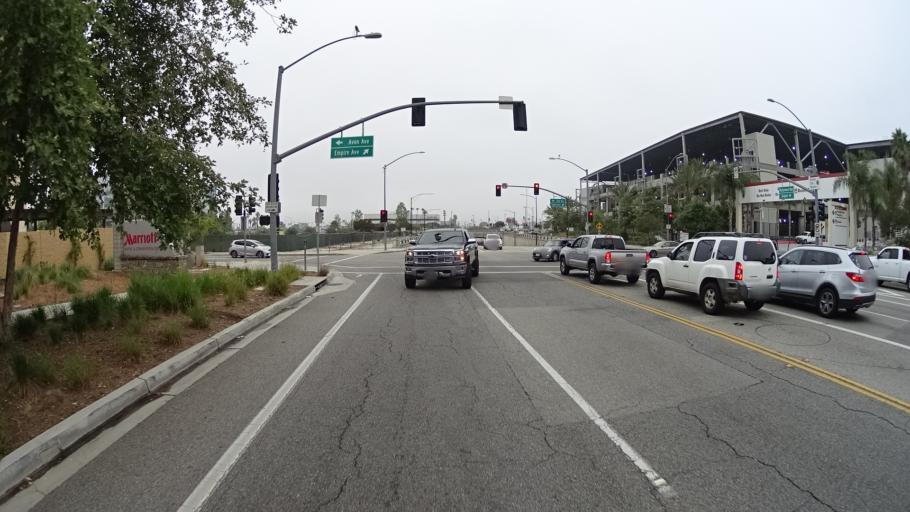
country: US
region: California
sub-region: Los Angeles County
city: North Hollywood
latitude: 34.1938
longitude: -118.3489
